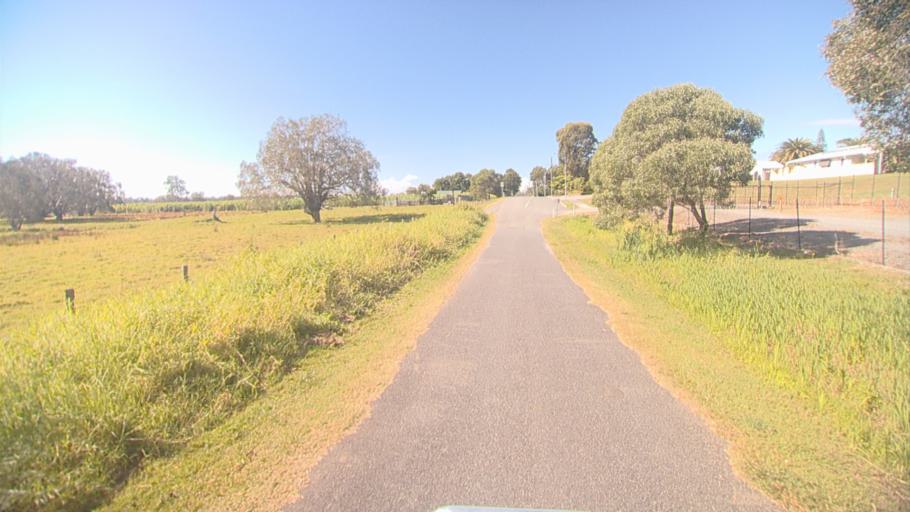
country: AU
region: Queensland
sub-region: Logan
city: Beenleigh
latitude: -27.6865
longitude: 153.2120
